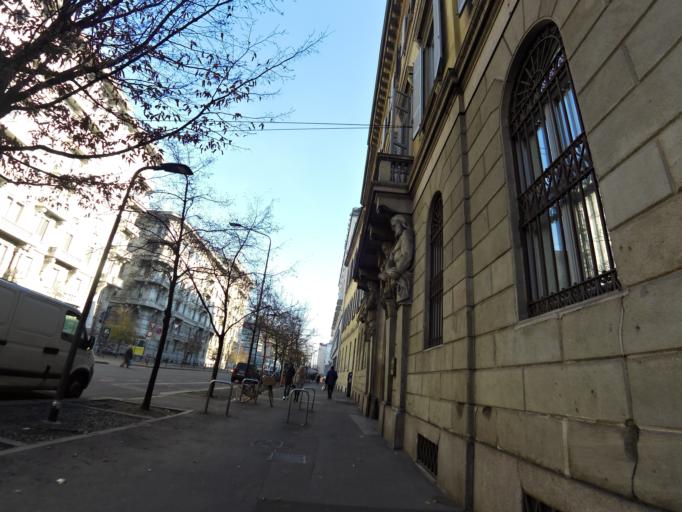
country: IT
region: Lombardy
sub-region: Citta metropolitana di Milano
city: Milano
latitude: 45.4626
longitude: 9.1989
